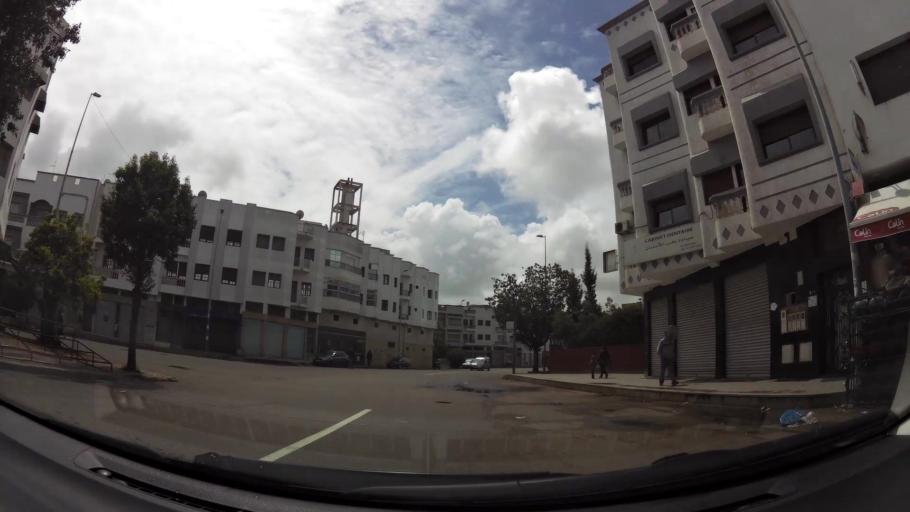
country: MA
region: Grand Casablanca
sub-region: Casablanca
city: Casablanca
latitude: 33.5460
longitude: -7.6823
